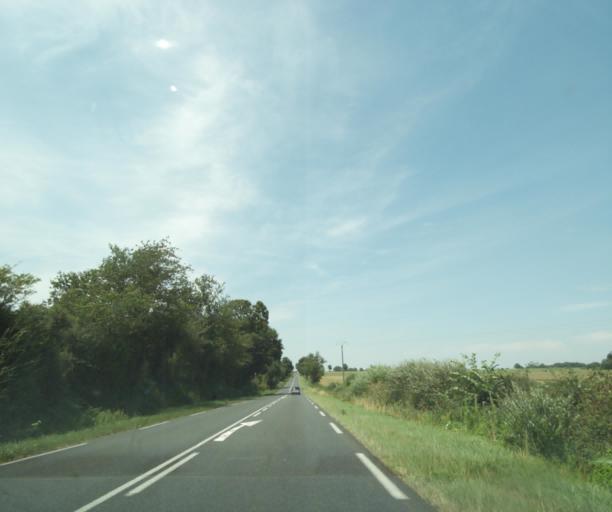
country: FR
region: Limousin
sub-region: Departement de la Haute-Vienne
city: Bussiere-Poitevine
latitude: 46.2915
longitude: 0.8454
